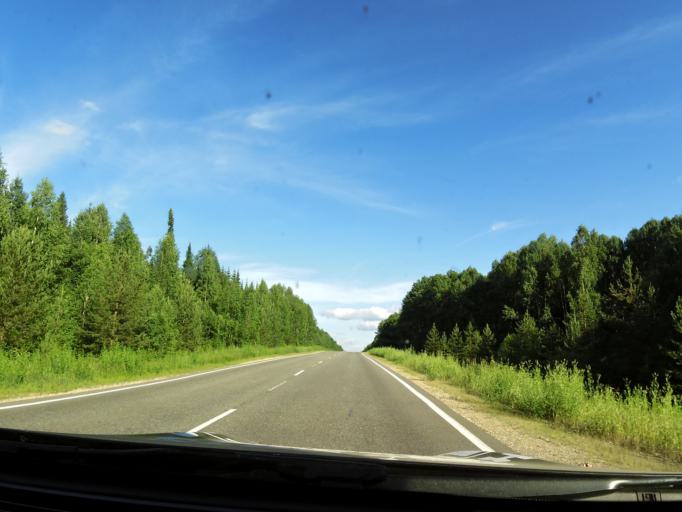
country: RU
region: Kirov
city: Chernaya Kholunitsa
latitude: 58.8183
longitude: 51.8157
